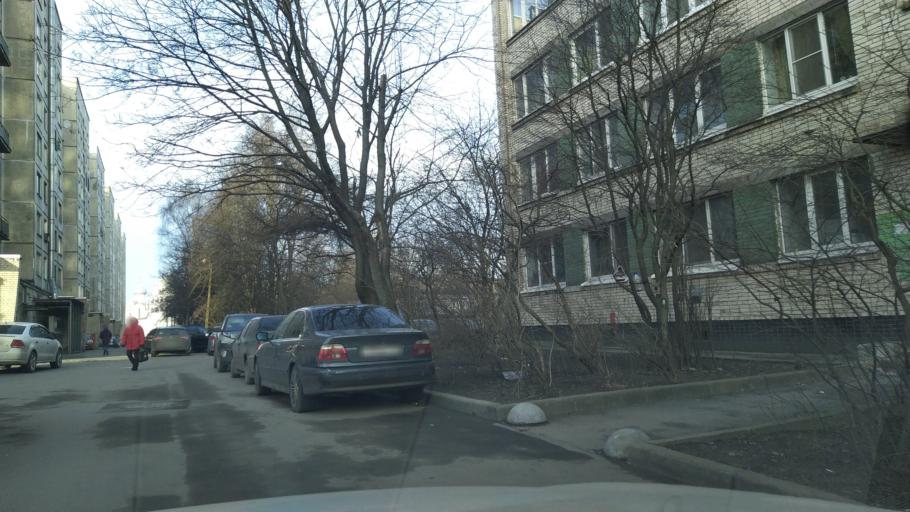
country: RU
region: Leningrad
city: Kalininskiy
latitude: 59.9778
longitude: 30.4205
